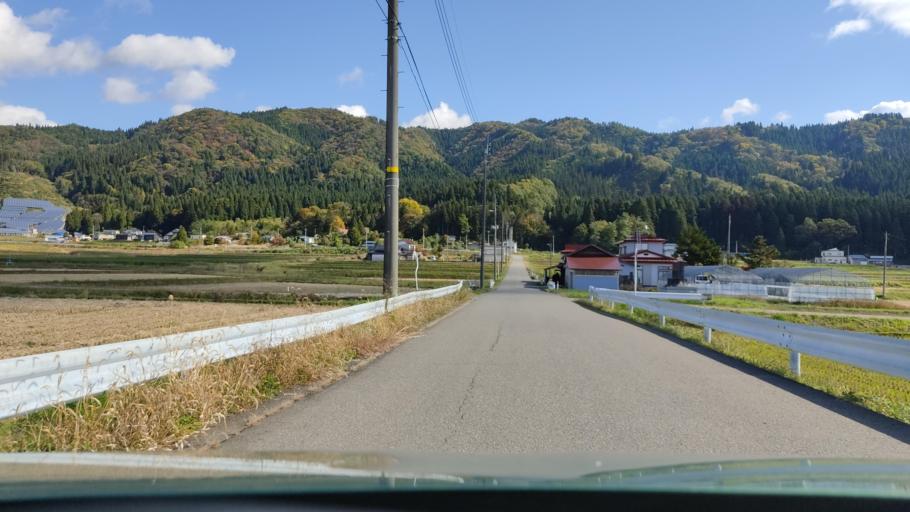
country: JP
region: Akita
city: Yokotemachi
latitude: 39.4016
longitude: 140.5857
